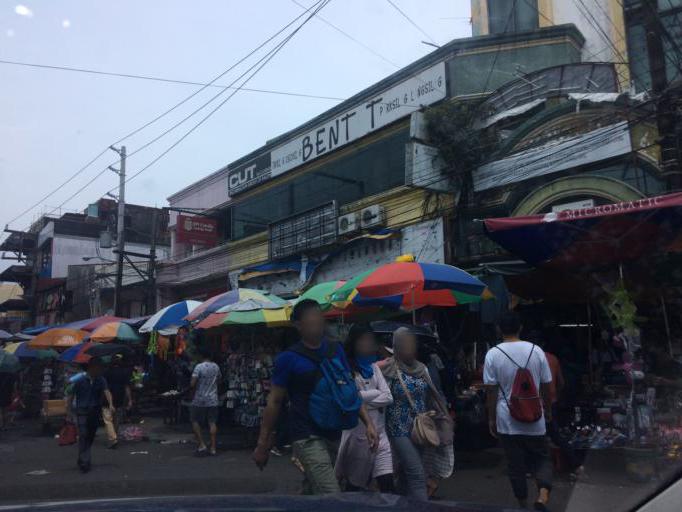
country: PH
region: Metro Manila
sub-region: Makati City
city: Makati City
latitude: 14.5323
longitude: 120.9969
